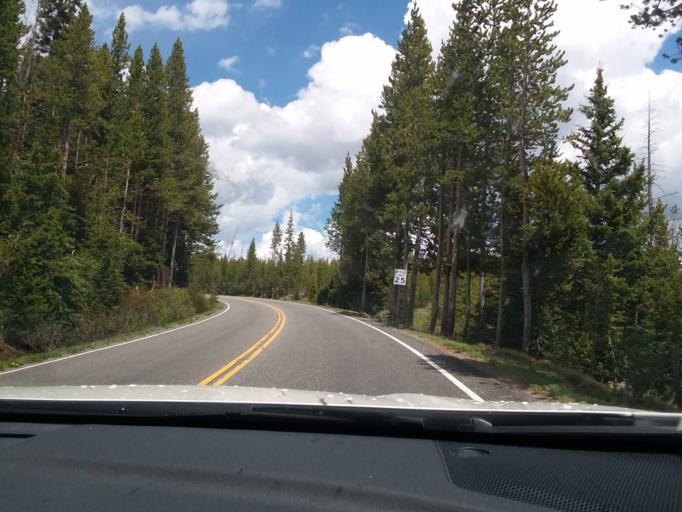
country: US
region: Montana
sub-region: Gallatin County
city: West Yellowstone
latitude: 44.2808
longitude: -110.6252
